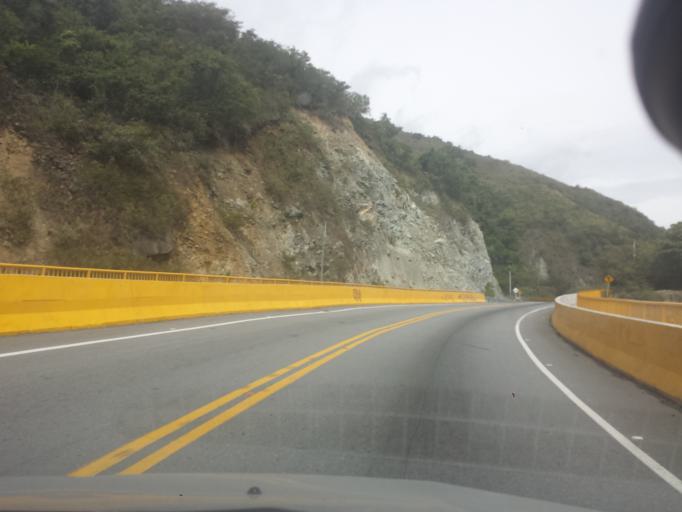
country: CO
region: Antioquia
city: Antioquia
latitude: 6.6117
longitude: -75.8487
